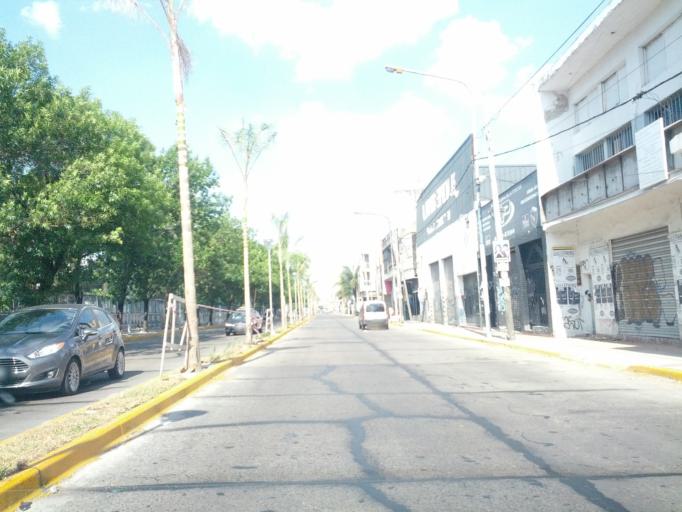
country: AR
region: Buenos Aires
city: San Justo
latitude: -34.6434
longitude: -58.5815
